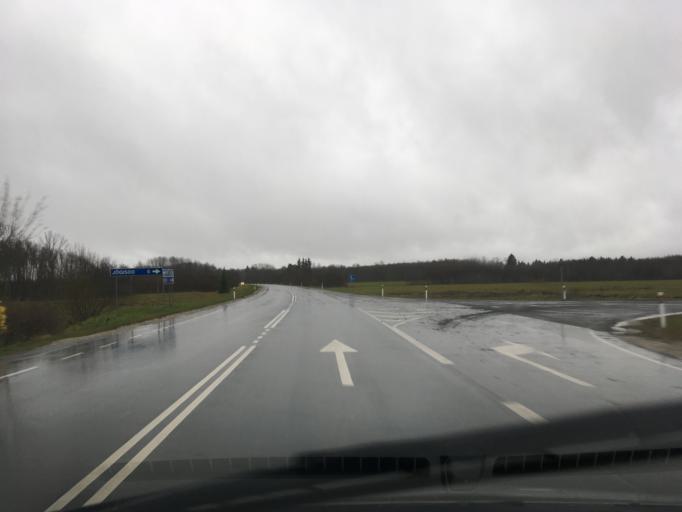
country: EE
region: Laeaene
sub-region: Lihula vald
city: Lihula
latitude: 58.8354
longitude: 24.0546
